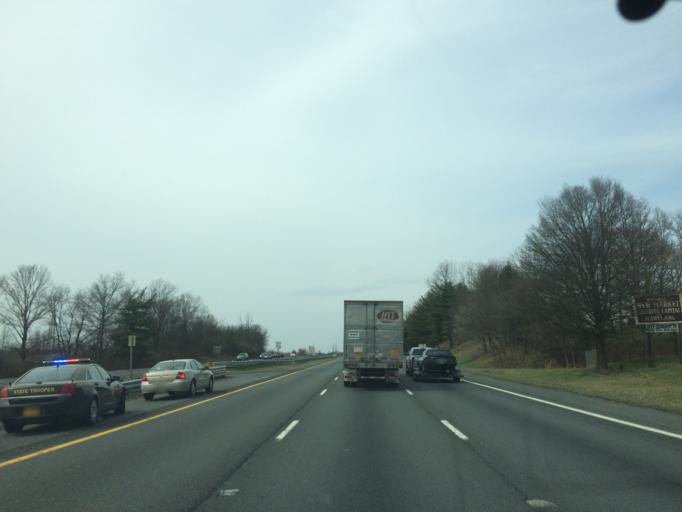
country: US
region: Maryland
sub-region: Frederick County
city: Green Valley
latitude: 39.3813
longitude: -77.2688
